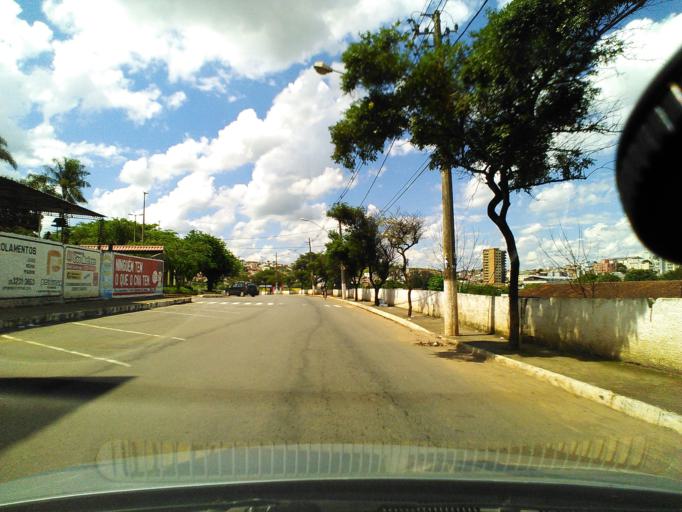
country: BR
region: Minas Gerais
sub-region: Tres Coracoes
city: Tres Coracoes
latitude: -21.7021
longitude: -45.2603
